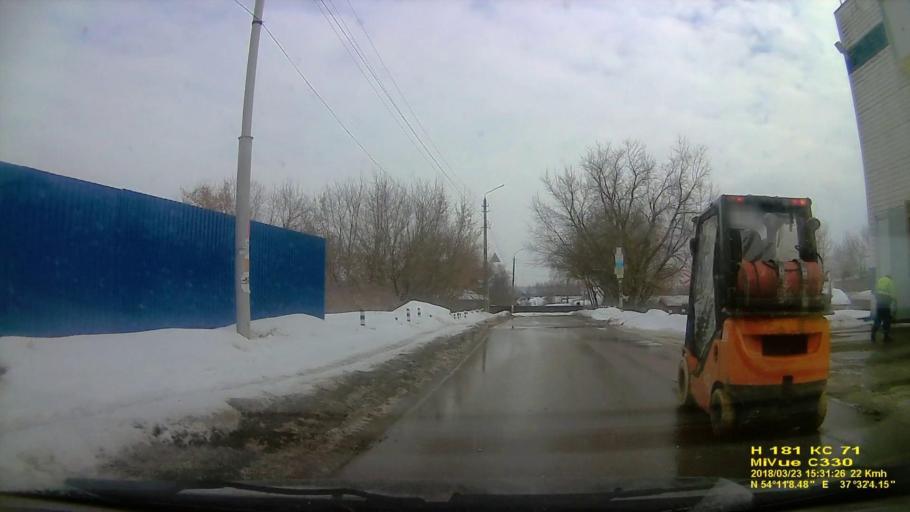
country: RU
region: Tula
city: Kosaya Gora
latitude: 54.1857
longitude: 37.5345
